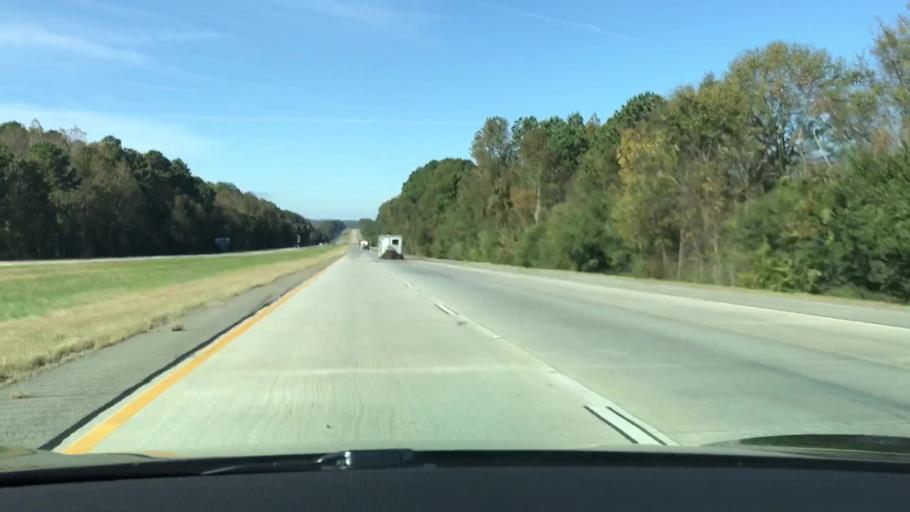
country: US
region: Georgia
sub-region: Greene County
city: Union Point
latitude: 33.5444
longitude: -83.0880
